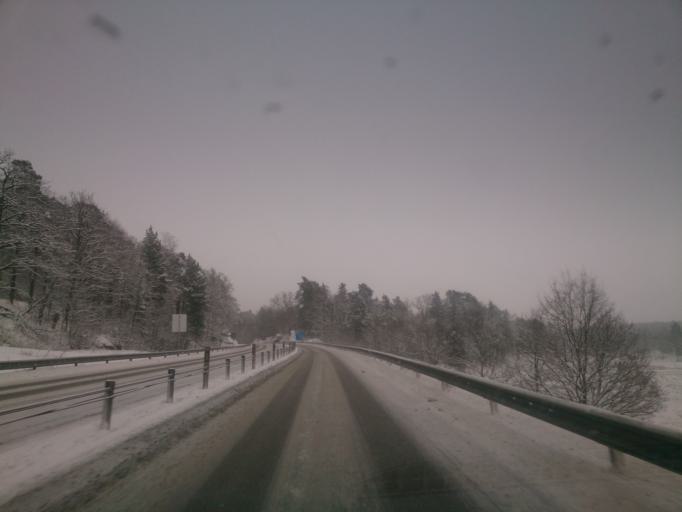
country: SE
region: OEstergoetland
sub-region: Norrkopings Kommun
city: Svartinge
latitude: 58.6960
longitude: 15.9070
